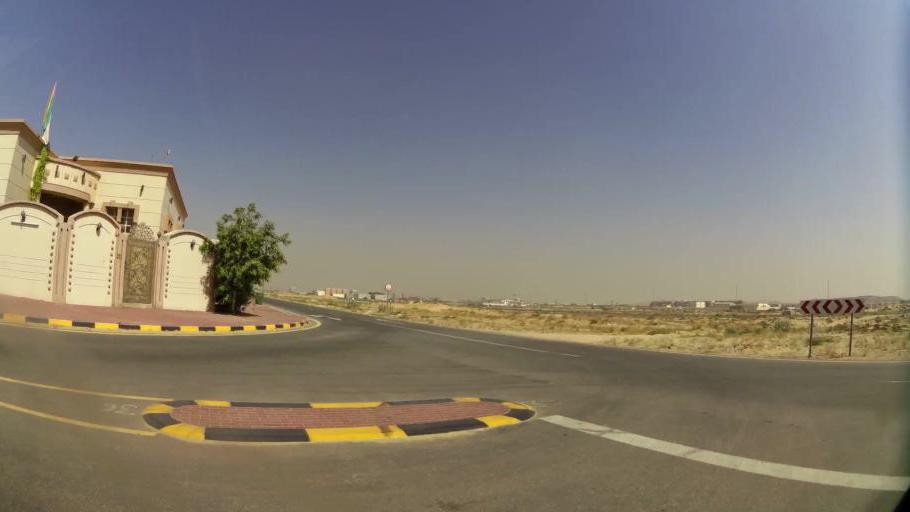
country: AE
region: Ajman
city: Ajman
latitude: 25.4133
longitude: 55.5516
